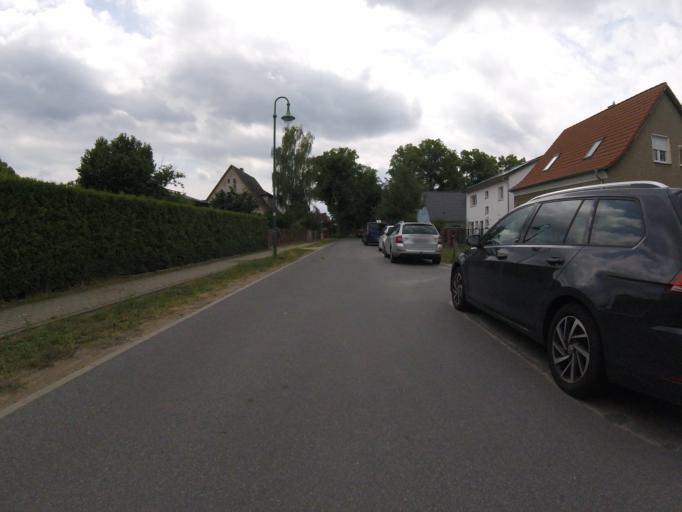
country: DE
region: Brandenburg
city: Konigs Wusterhausen
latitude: 52.2807
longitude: 13.6405
